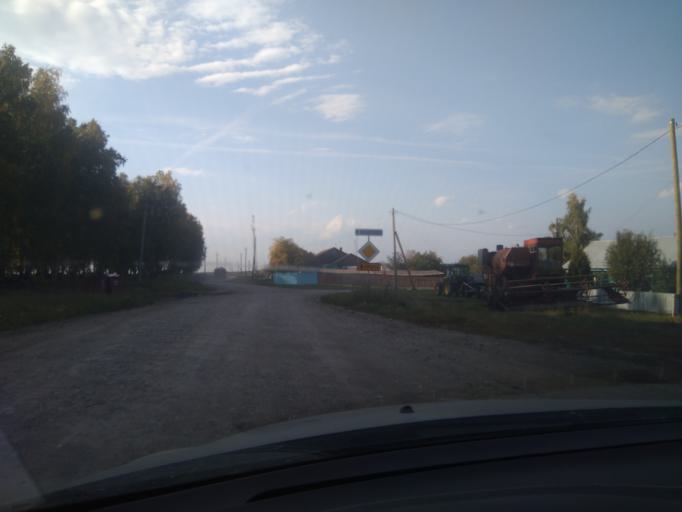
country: RU
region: Sverdlovsk
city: Pokrovskoye
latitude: 56.4308
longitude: 61.5936
